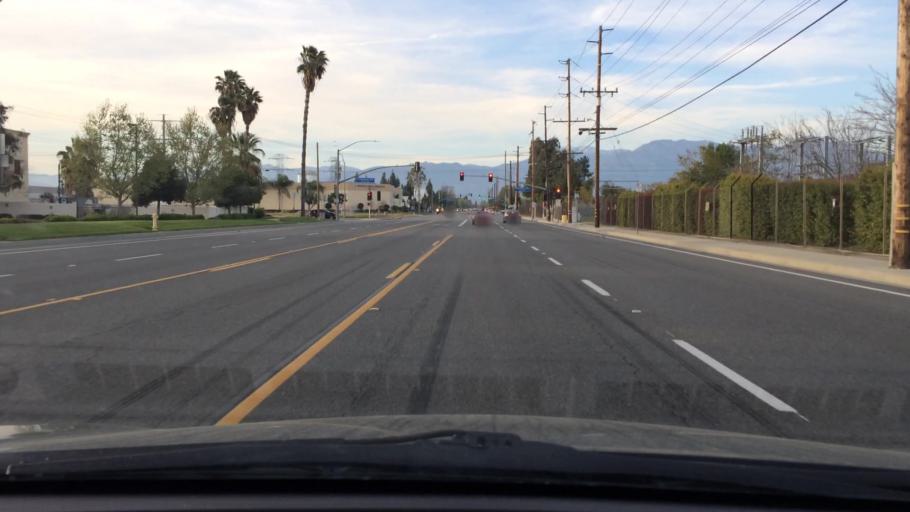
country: US
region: California
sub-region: San Bernardino County
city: Chino
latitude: 33.9889
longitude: -117.6890
